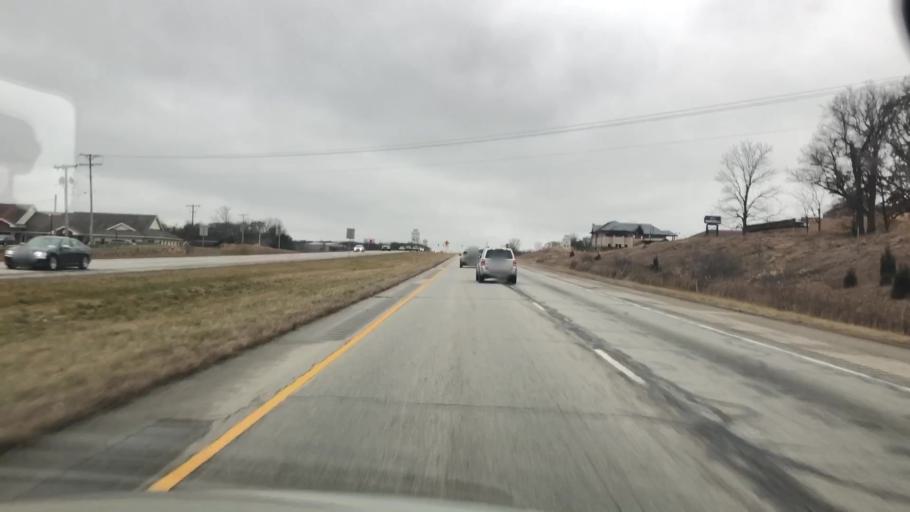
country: US
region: Indiana
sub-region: Kosciusko County
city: Winona Lake
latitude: 41.2486
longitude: -85.8246
